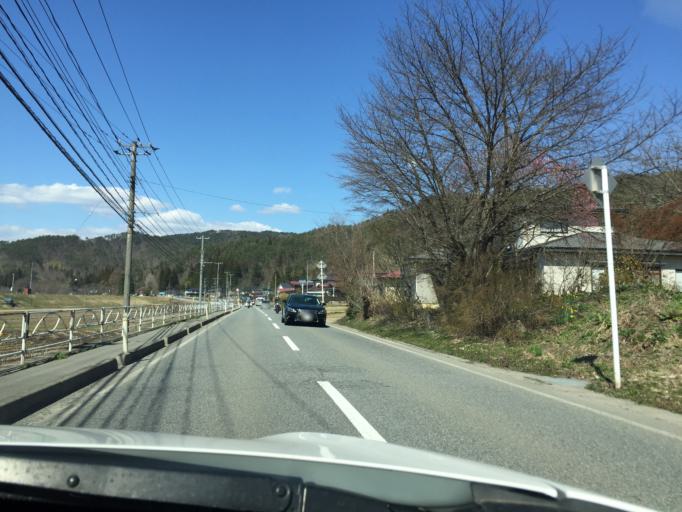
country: JP
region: Yamagata
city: Nagai
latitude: 38.1949
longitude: 140.1014
